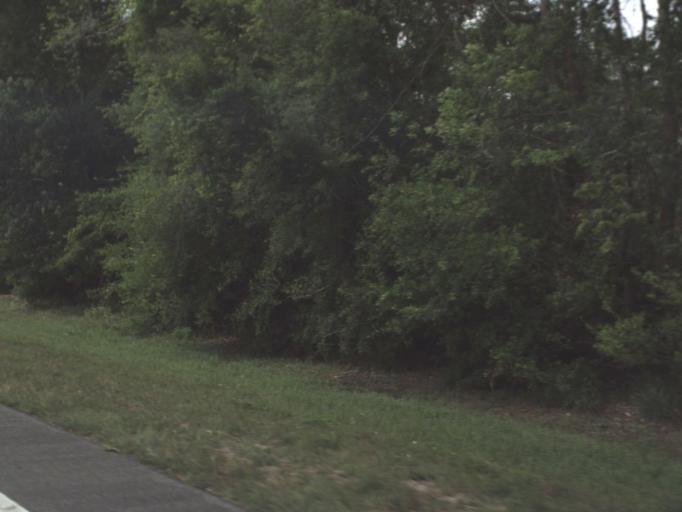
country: US
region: Florida
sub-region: Flagler County
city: Bunnell
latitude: 29.4756
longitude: -81.3316
